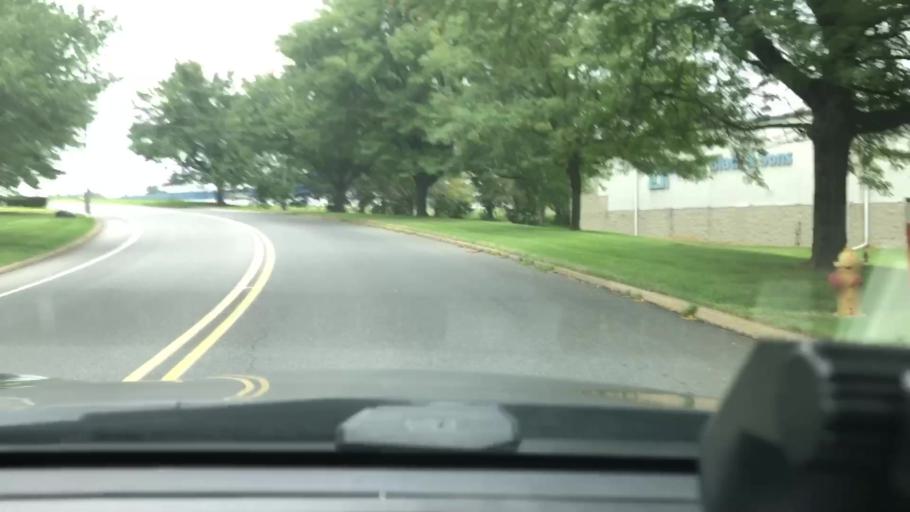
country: US
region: Pennsylvania
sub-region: Lehigh County
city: Fullerton
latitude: 40.6426
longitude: -75.4391
